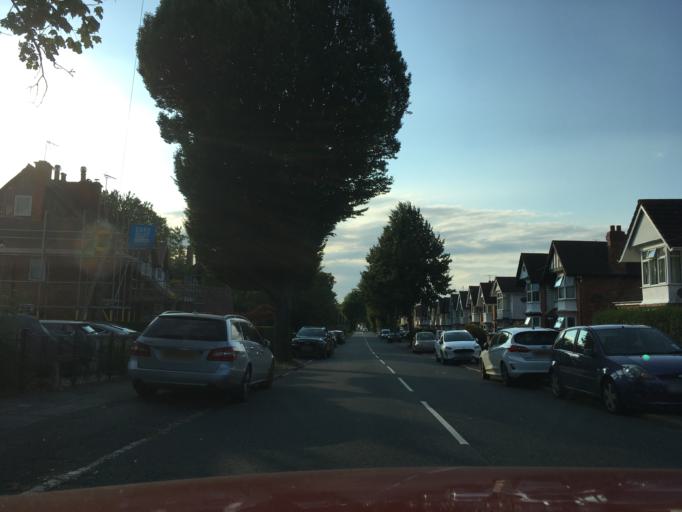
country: GB
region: England
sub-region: Gloucestershire
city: Gloucester
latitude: 51.8448
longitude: -2.2475
